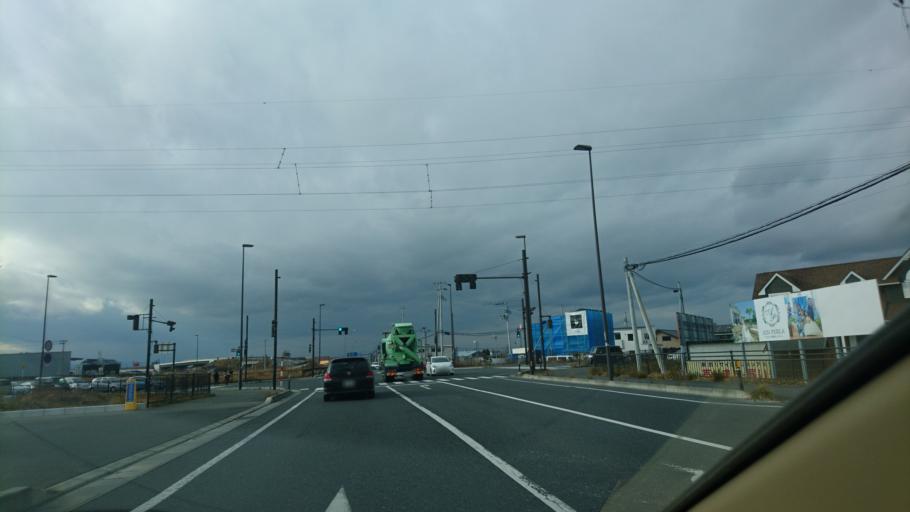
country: JP
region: Miyagi
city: Furukawa
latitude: 38.5685
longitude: 140.9916
